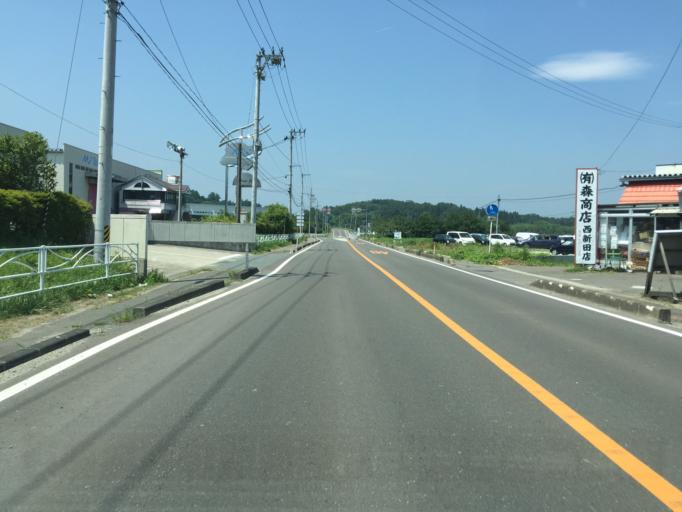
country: JP
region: Miyagi
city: Marumori
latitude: 37.9046
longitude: 140.7959
